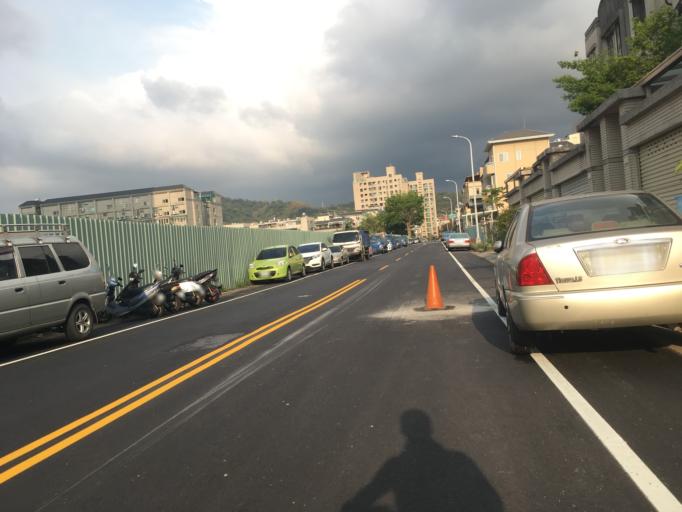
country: TW
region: Taiwan
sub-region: Taichung City
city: Taichung
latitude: 24.1812
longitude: 120.7156
